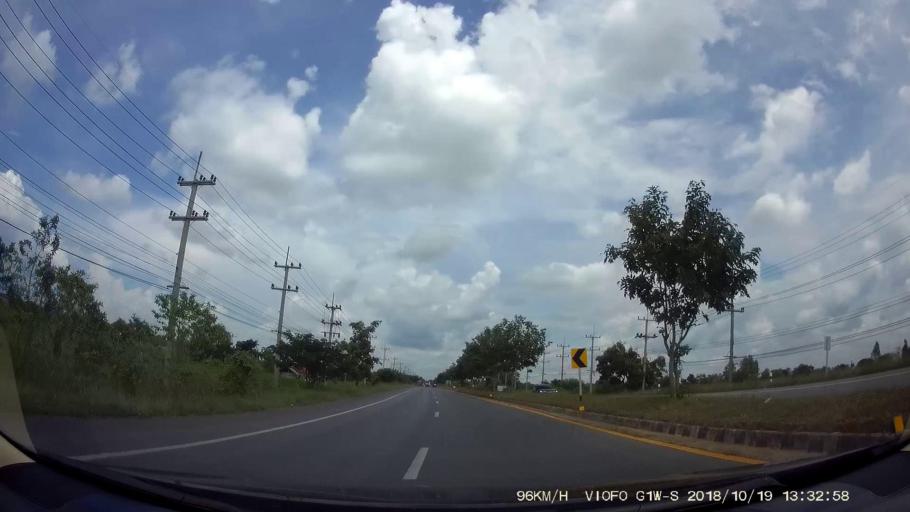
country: TH
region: Chaiyaphum
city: Chatturat
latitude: 15.5772
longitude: 101.8901
